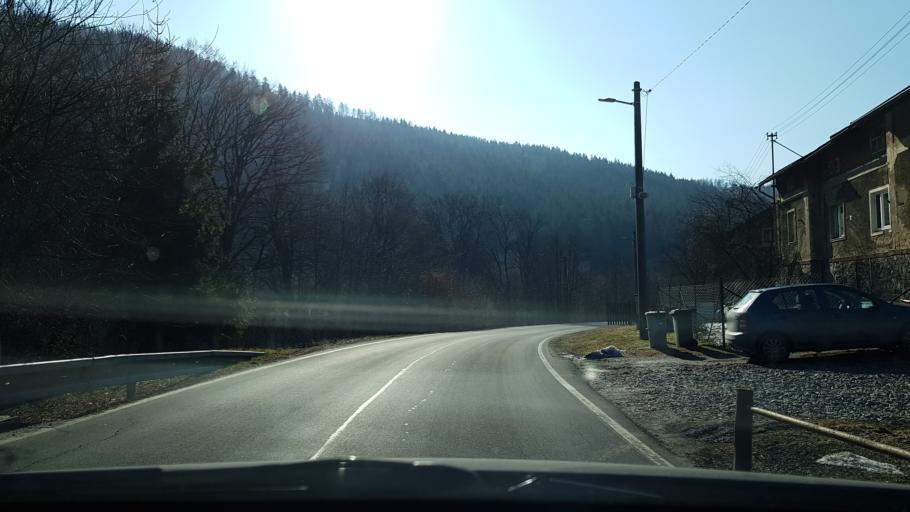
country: CZ
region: Olomoucky
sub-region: Okres Sumperk
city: Hanusovice
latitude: 50.0629
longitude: 16.9243
